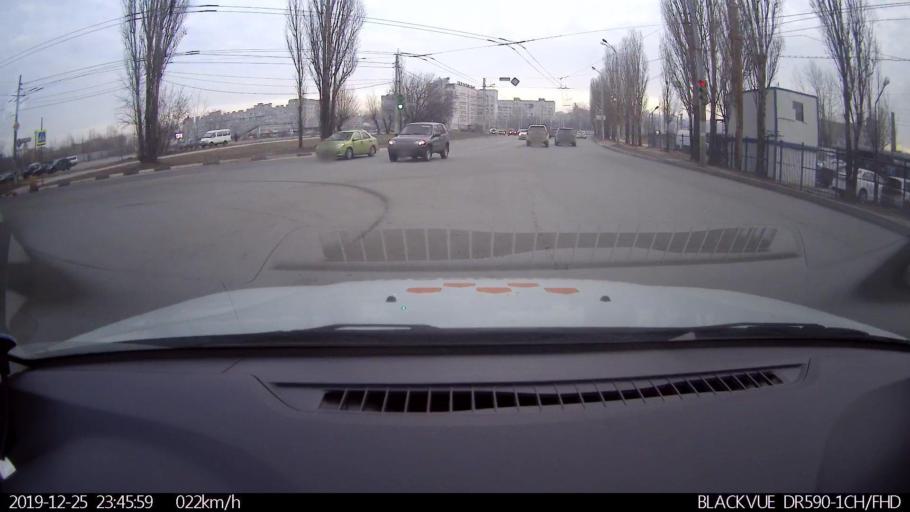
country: RU
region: Nizjnij Novgorod
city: Nizhniy Novgorod
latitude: 56.3304
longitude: 43.9451
